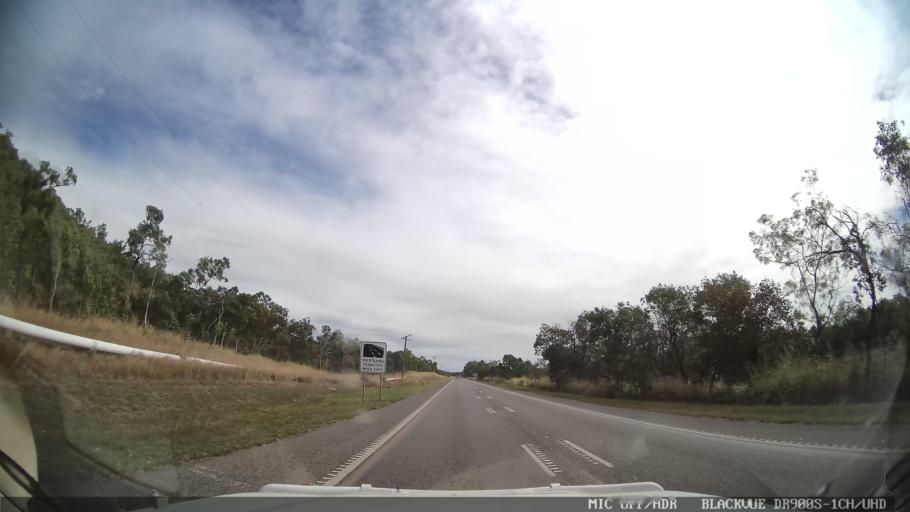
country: AU
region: Queensland
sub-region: Hinchinbrook
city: Ingham
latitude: -19.0067
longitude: 146.3606
